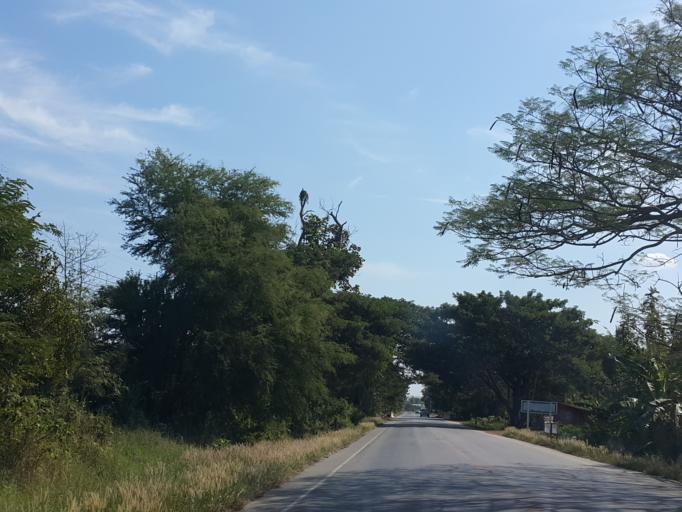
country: TH
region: Sukhothai
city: Thung Saliam
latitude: 17.3304
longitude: 99.6225
